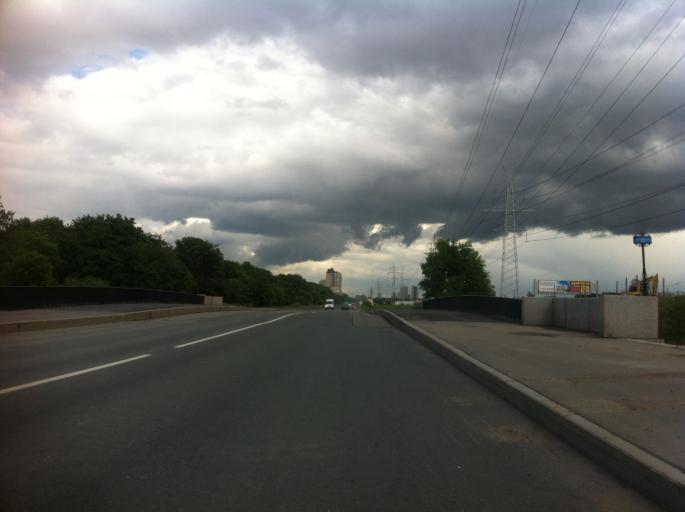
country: RU
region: St.-Petersburg
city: Sosnovaya Polyana
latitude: 59.8475
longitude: 30.1579
